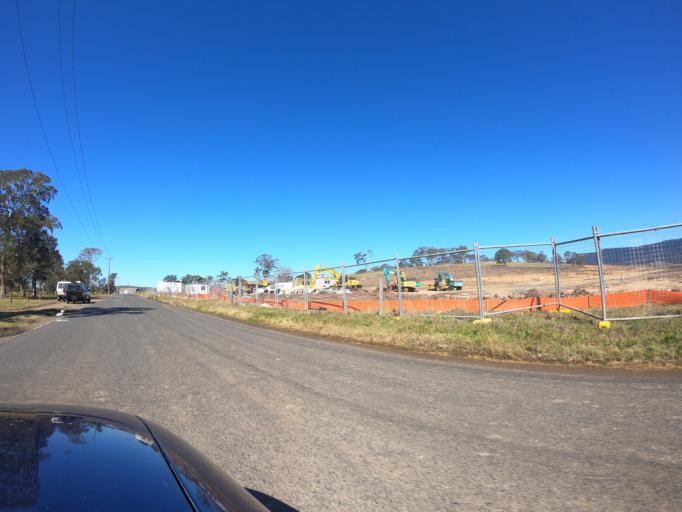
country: AU
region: New South Wales
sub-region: Wollongong
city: Dapto
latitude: -34.4767
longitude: 150.7911
